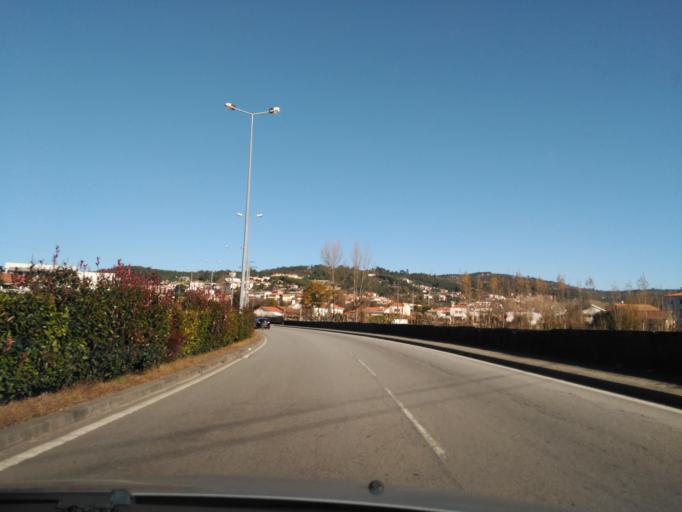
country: PT
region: Braga
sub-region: Braga
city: Adaufe
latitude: 41.5682
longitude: -8.3697
